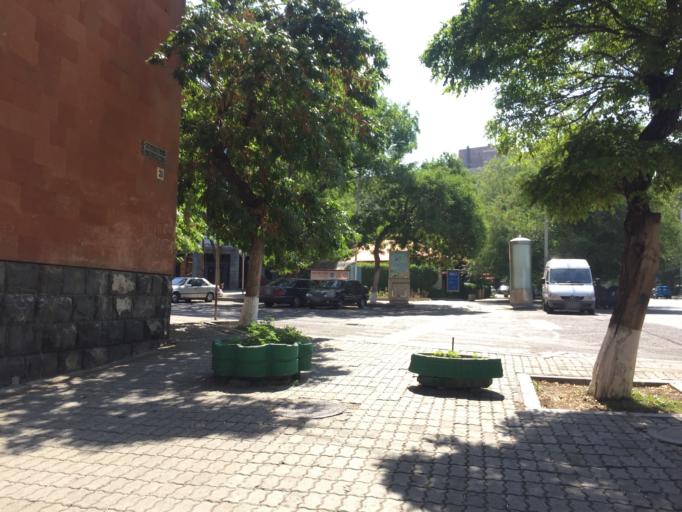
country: AM
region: Yerevan
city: Yerevan
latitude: 40.1887
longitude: 44.5190
